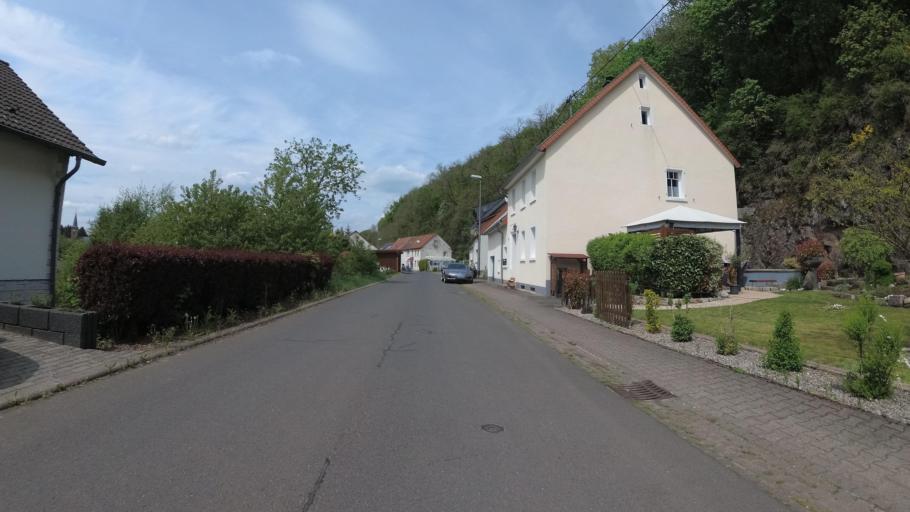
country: DE
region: Rheinland-Pfalz
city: Fohren-Linden
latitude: 49.5759
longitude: 7.2958
